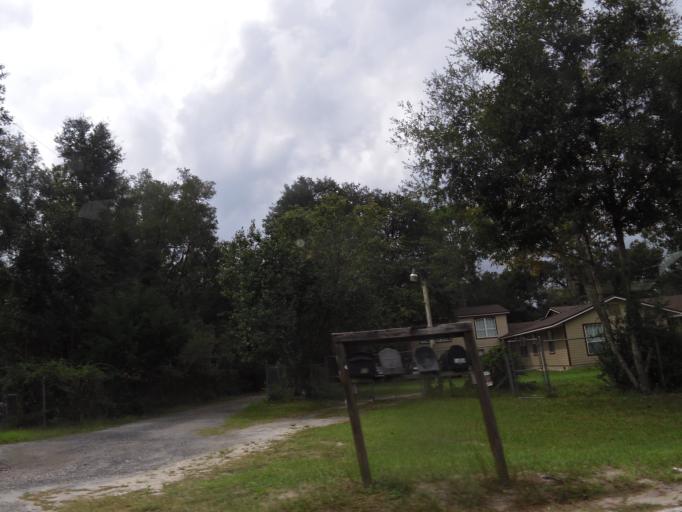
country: US
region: Florida
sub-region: Clay County
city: Middleburg
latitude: 30.1231
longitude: -81.9618
